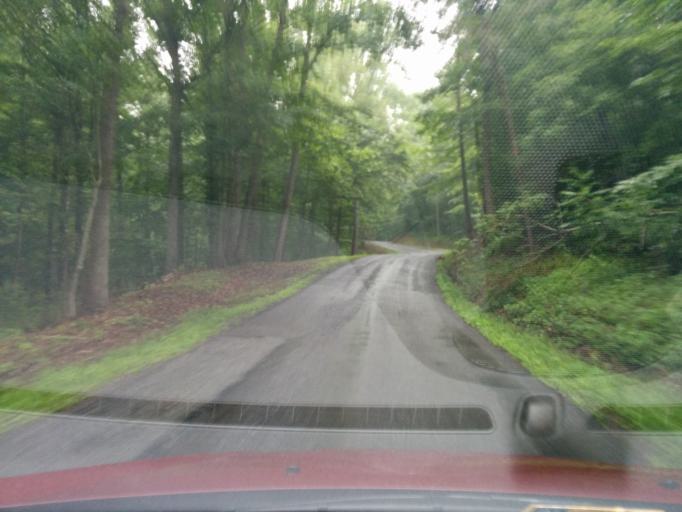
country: US
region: Virginia
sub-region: Rockbridge County
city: East Lexington
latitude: 37.8597
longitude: -79.4219
